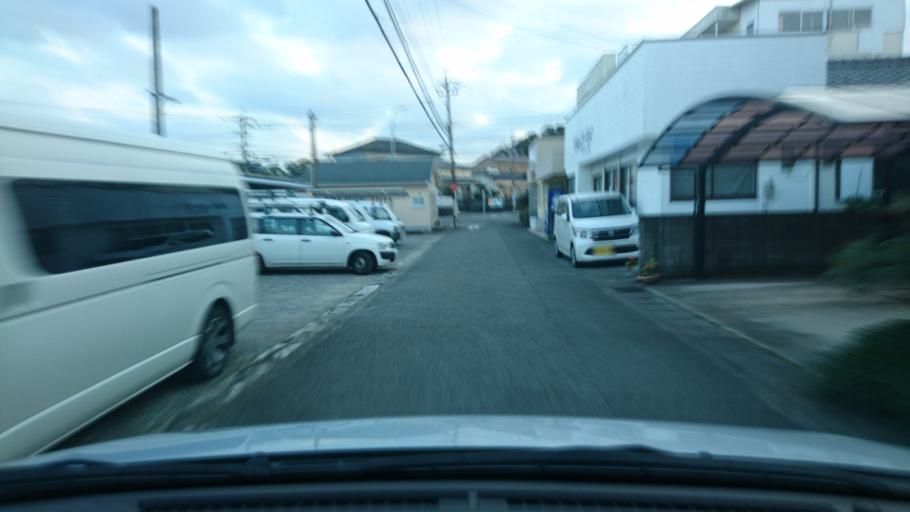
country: JP
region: Miyazaki
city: Miyazaki-shi
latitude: 31.8582
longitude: 131.4240
